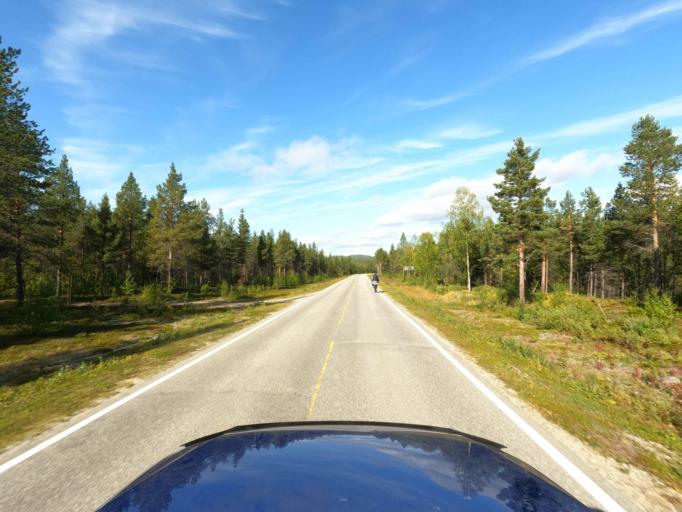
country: NO
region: Finnmark Fylke
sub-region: Porsanger
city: Lakselv
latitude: 69.8153
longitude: 25.1588
